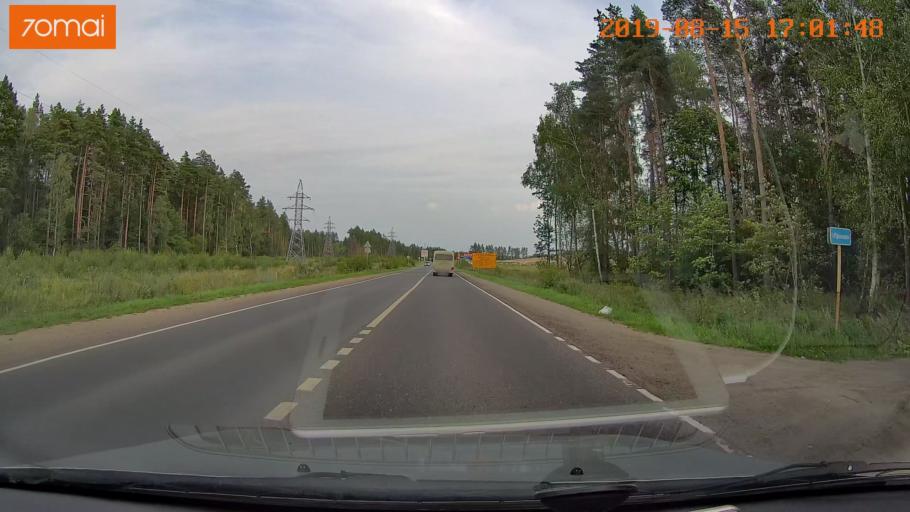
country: RU
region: Moskovskaya
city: Malyshevo
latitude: 55.4880
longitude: 38.3810
